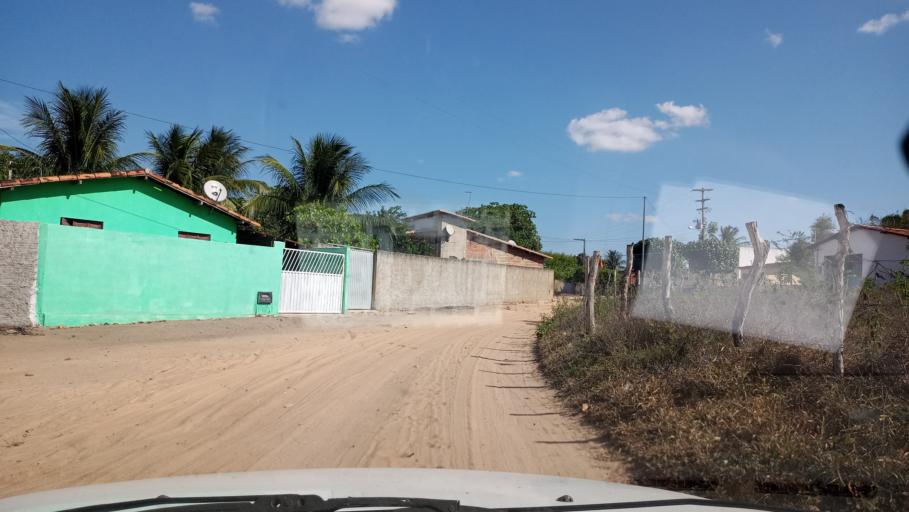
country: BR
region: Rio Grande do Norte
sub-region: Brejinho
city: Brejinho
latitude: -6.1731
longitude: -35.4678
